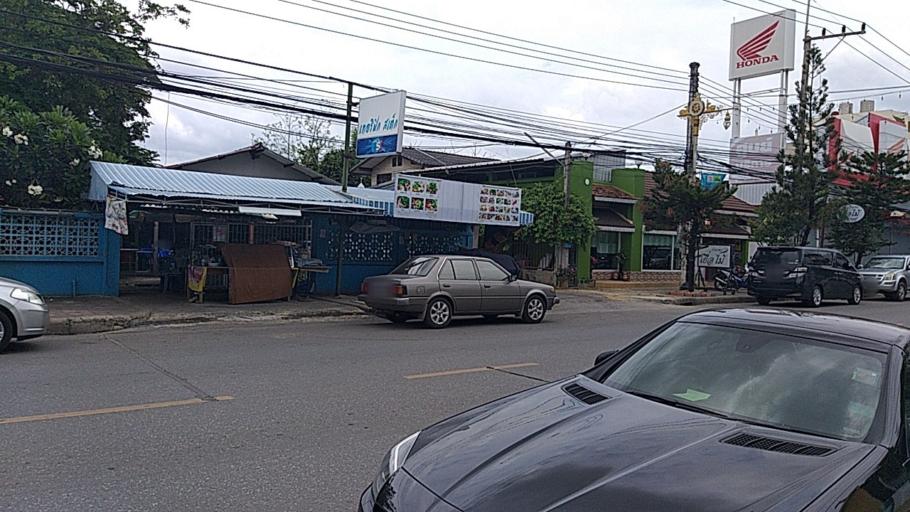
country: TH
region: Nakhon Pathom
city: Nakhon Pathom
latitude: 13.8196
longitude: 100.0541
